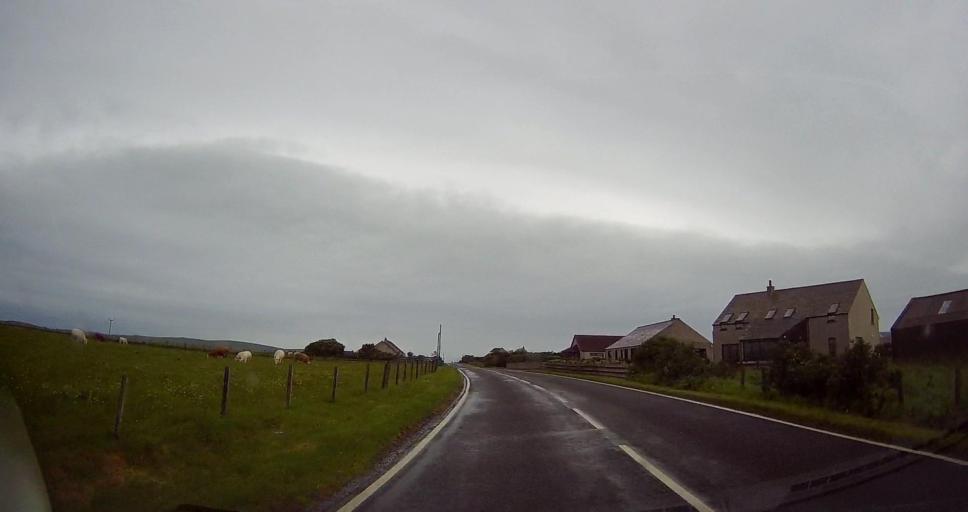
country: GB
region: Scotland
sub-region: Orkney Islands
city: Stromness
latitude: 59.0718
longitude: -3.2375
